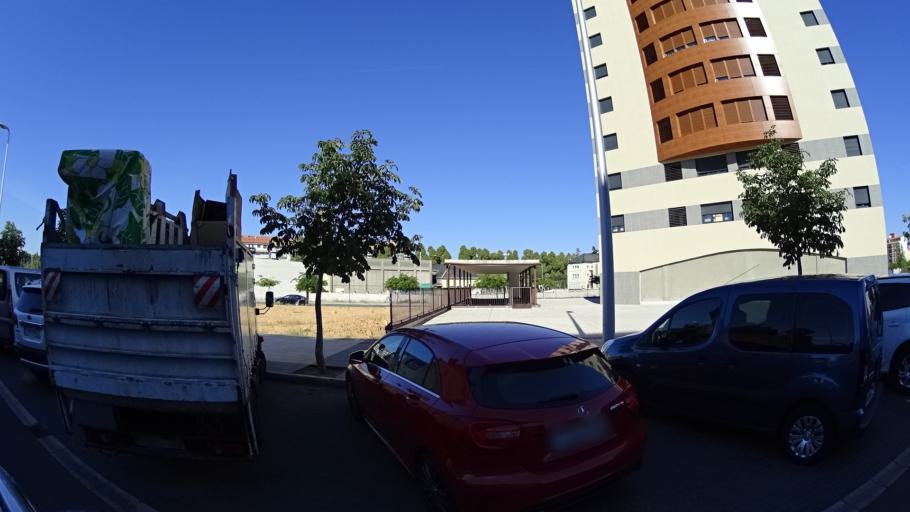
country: ES
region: Castille and Leon
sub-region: Provincia de Leon
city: Leon
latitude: 42.5831
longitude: -5.5653
